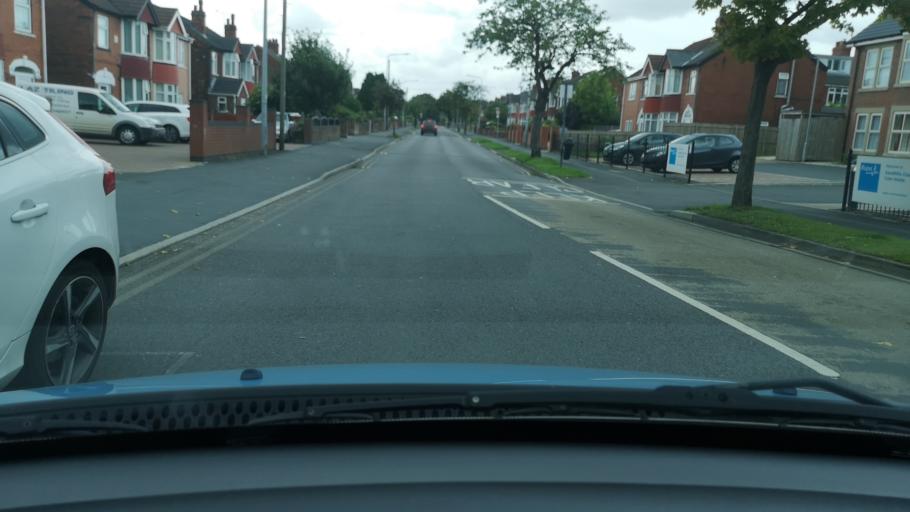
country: GB
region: England
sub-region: North Lincolnshire
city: Scunthorpe
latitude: 53.5904
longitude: -0.6610
